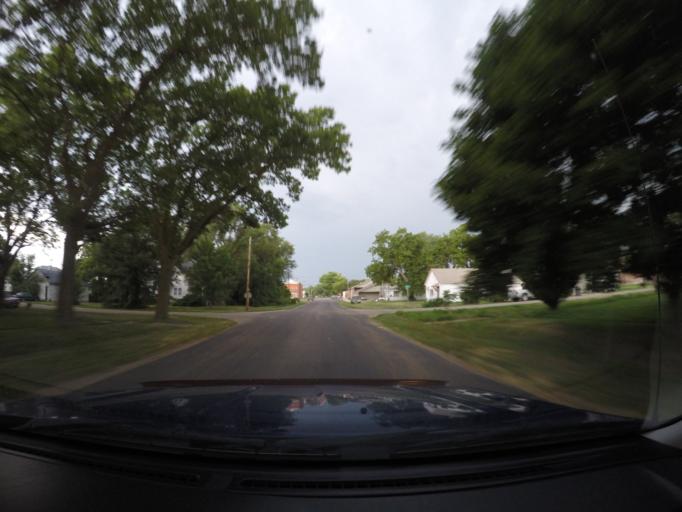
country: US
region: Nebraska
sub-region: Buffalo County
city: Kearney
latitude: 40.8383
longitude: -99.2685
